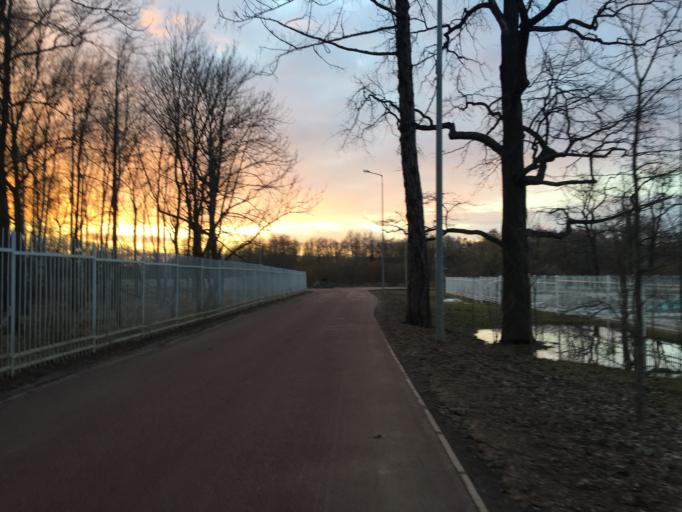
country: RU
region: St.-Petersburg
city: Pushkin
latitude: 59.7258
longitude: 30.3782
